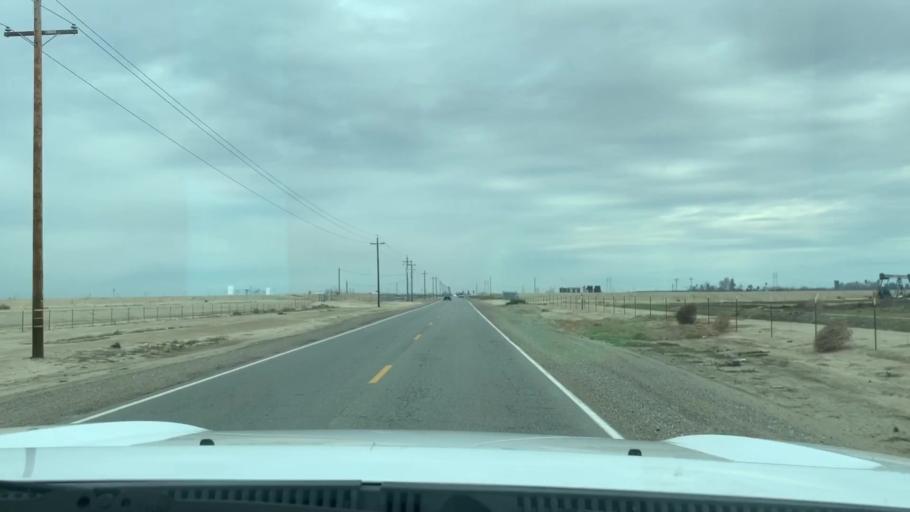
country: US
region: California
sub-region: Kern County
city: Rosedale
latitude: 35.3447
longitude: -119.2522
